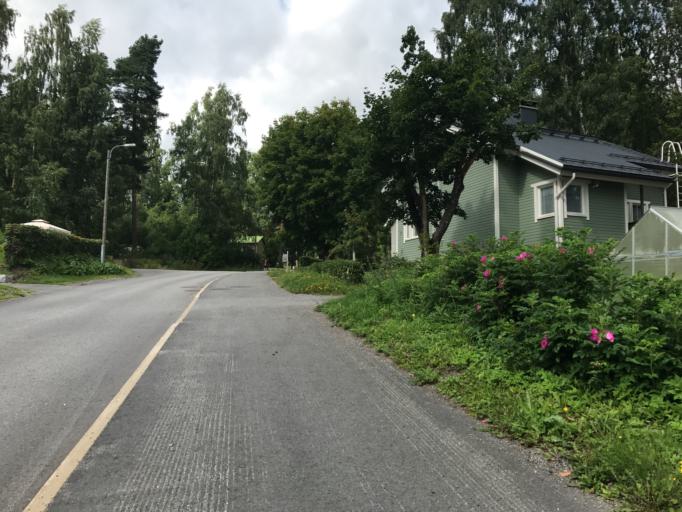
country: FI
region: Pirkanmaa
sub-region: Etelae-Pirkanmaa
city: Valkeakoski
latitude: 61.2579
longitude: 24.0444
